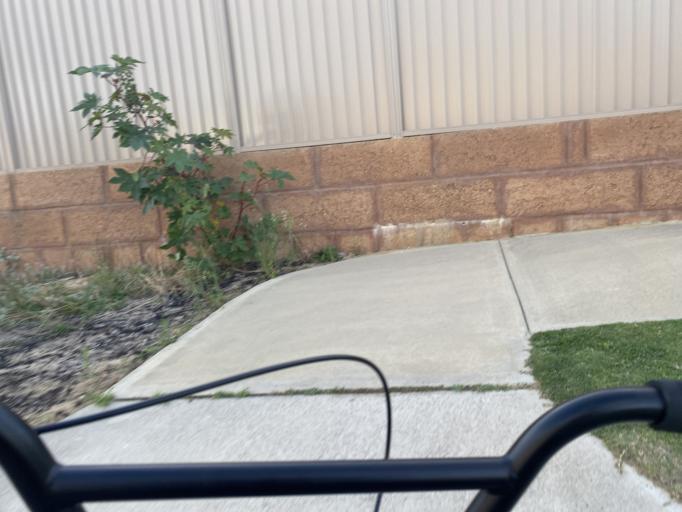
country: AU
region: Western Australia
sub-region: Kalamunda
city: Maida Vale
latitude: -31.9711
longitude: 116.0085
